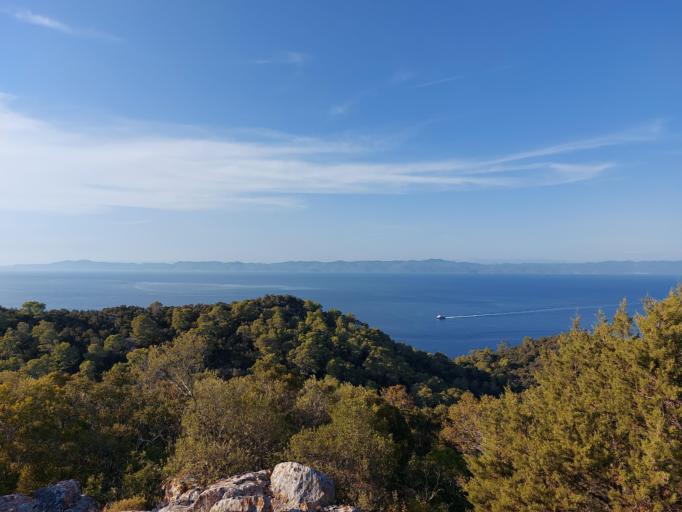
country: HR
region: Dubrovacko-Neretvanska
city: Smokvica
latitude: 42.7672
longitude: 16.8067
